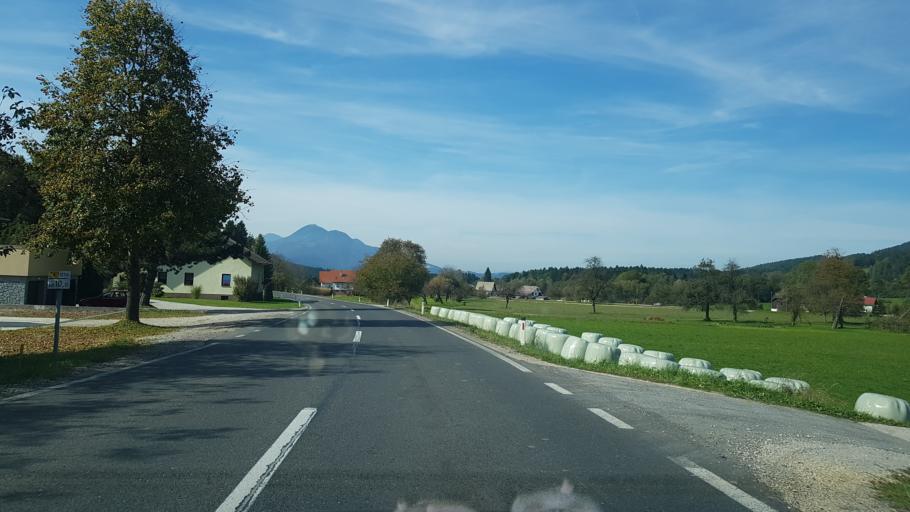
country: SI
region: Mislinja
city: Mislinja
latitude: 46.4446
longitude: 15.1884
